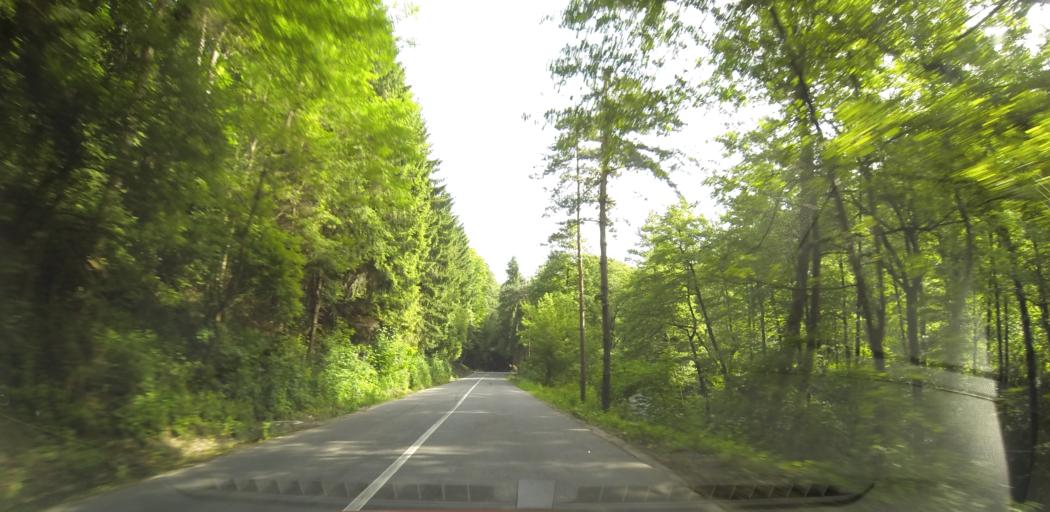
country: RO
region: Valcea
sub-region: Oras Baile Olanesti
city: Livadia
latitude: 45.1953
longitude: 24.2503
